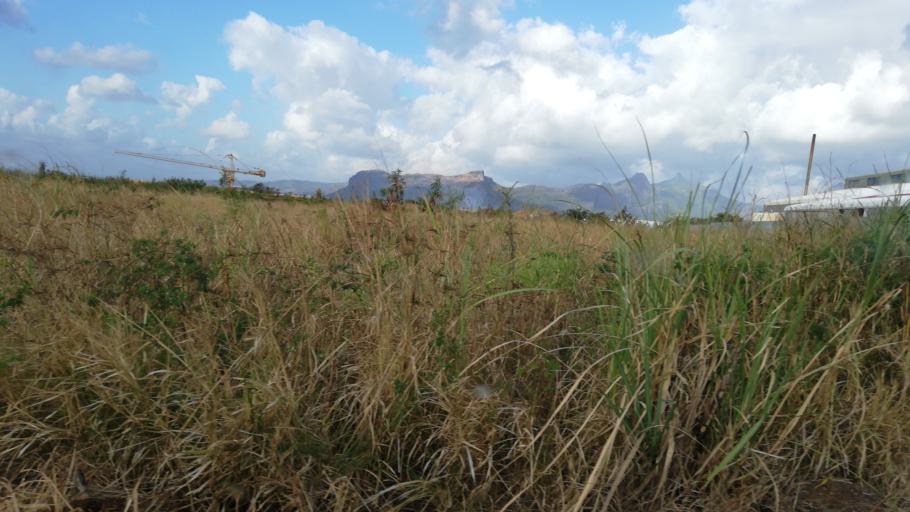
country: MU
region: Black River
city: Petite Riviere
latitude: -20.1837
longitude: 57.4434
